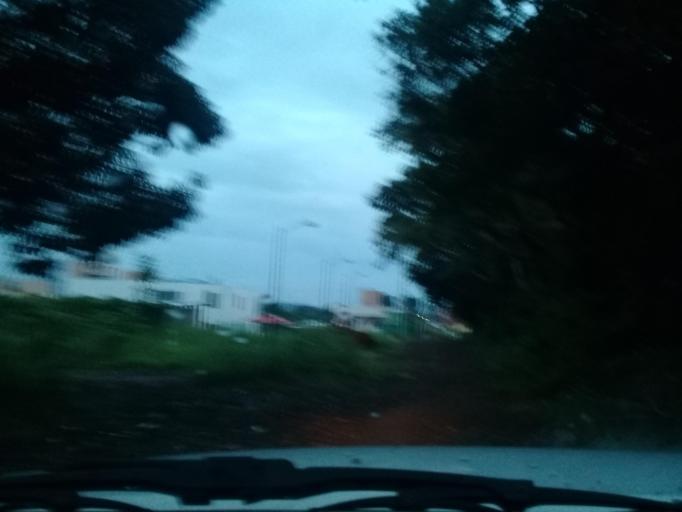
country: MX
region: Veracruz
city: San Andres Tuxtla
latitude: 18.4403
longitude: -95.2233
